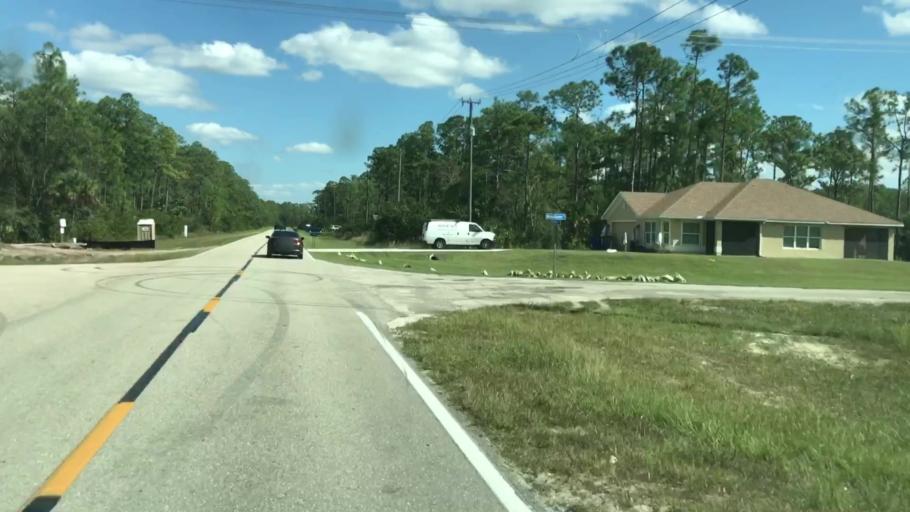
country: US
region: Florida
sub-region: Lee County
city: Alva
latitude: 26.6775
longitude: -81.6114
